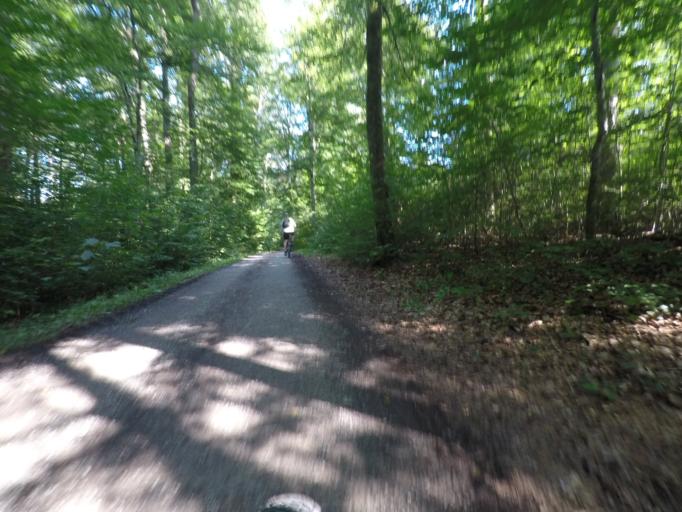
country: DE
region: Baden-Wuerttemberg
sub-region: Regierungsbezirk Stuttgart
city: Hildrizhausen
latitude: 48.6486
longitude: 8.9725
